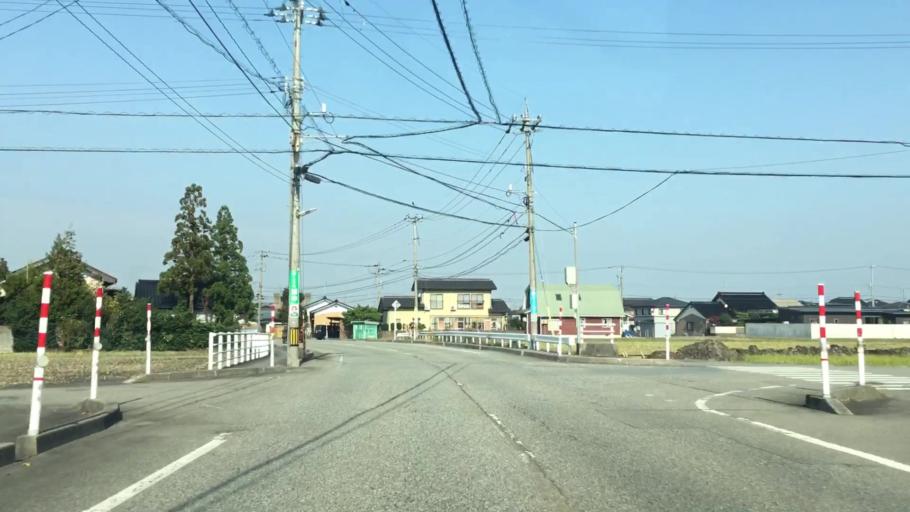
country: JP
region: Toyama
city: Yatsuomachi-higashikumisaka
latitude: 36.5705
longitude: 137.1967
